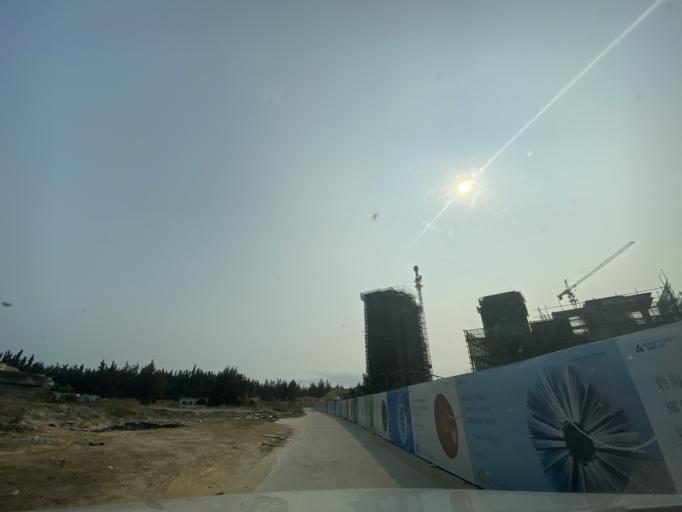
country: CN
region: Hainan
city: Yingzhou
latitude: 18.3942
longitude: 109.8561
